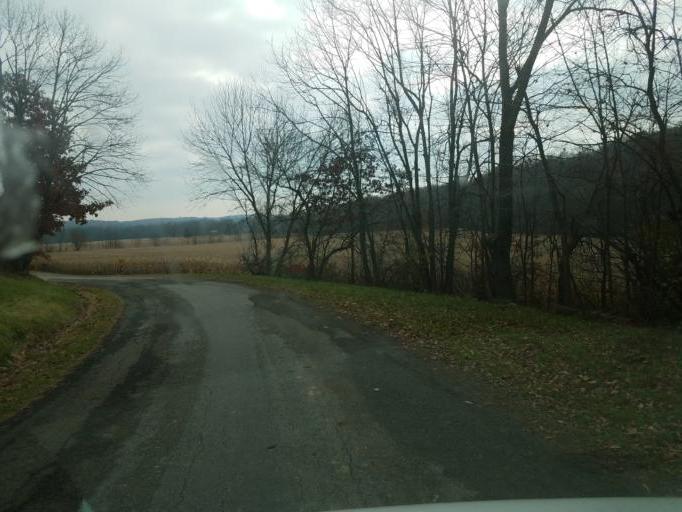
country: US
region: Ohio
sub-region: Knox County
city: Danville
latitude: 40.5099
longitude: -82.3110
